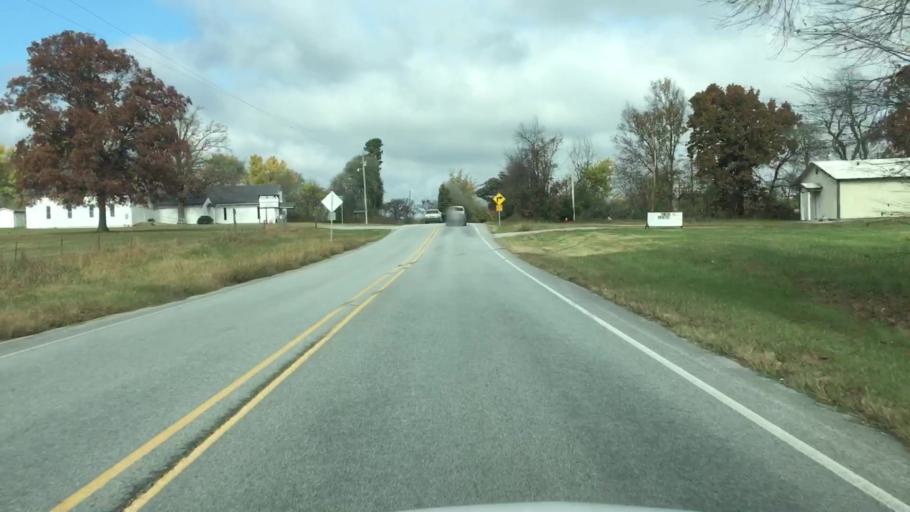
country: US
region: Arkansas
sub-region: Benton County
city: Centerton
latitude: 36.2968
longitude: -94.3409
